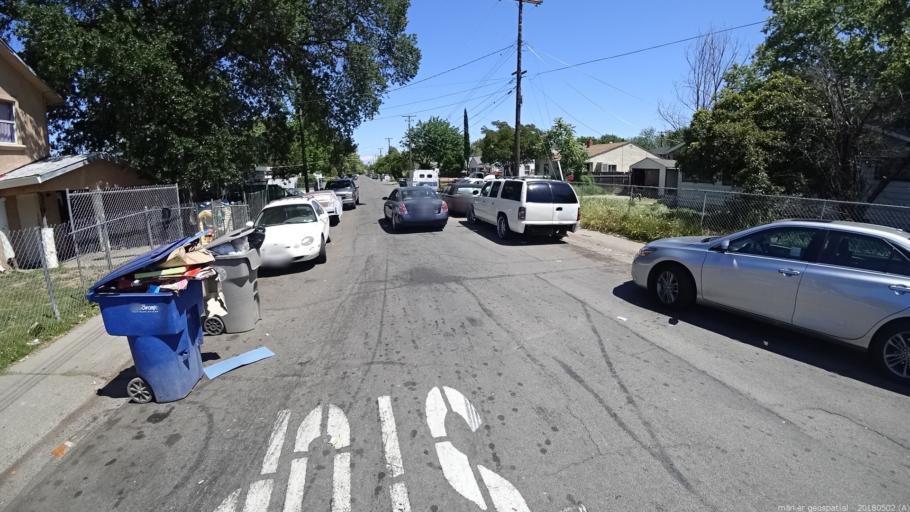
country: US
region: California
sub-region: Sacramento County
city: Sacramento
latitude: 38.6184
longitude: -121.4460
